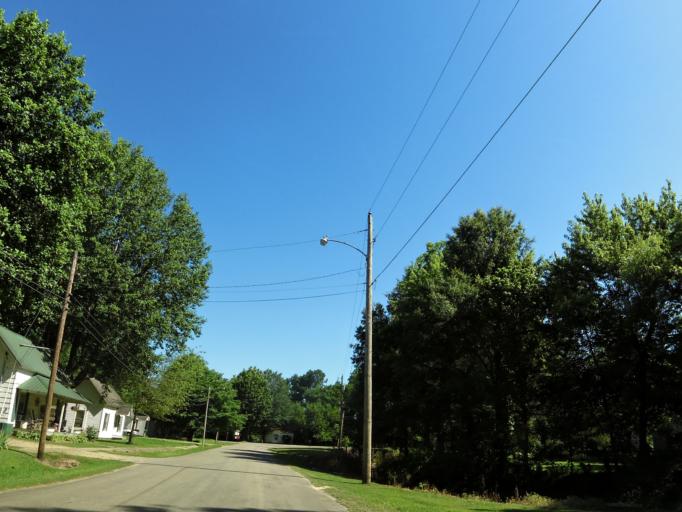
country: US
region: Arkansas
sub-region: Clay County
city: Piggott
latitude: 36.3809
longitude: -90.1952
